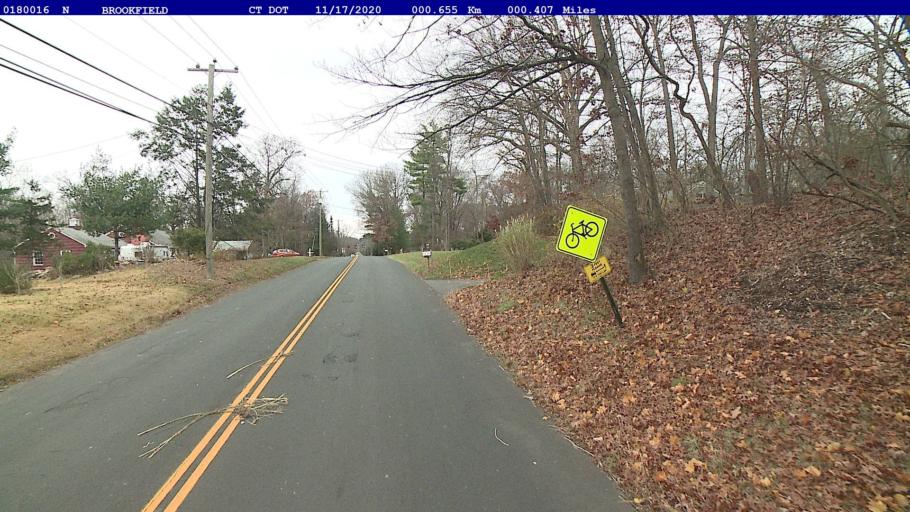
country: US
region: Connecticut
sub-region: Fairfield County
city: Danbury
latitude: 41.4394
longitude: -73.4132
